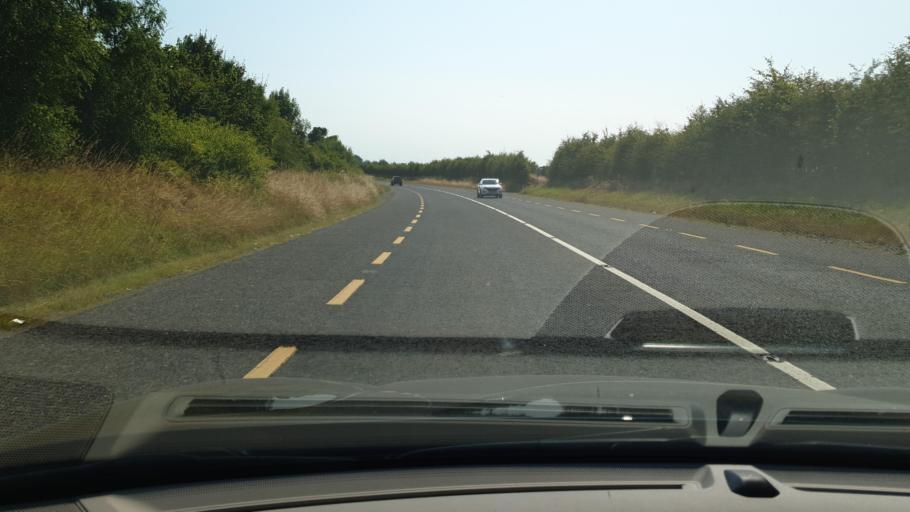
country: IE
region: Leinster
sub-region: An Mhi
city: Dunshaughlin
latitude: 53.5148
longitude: -6.5563
